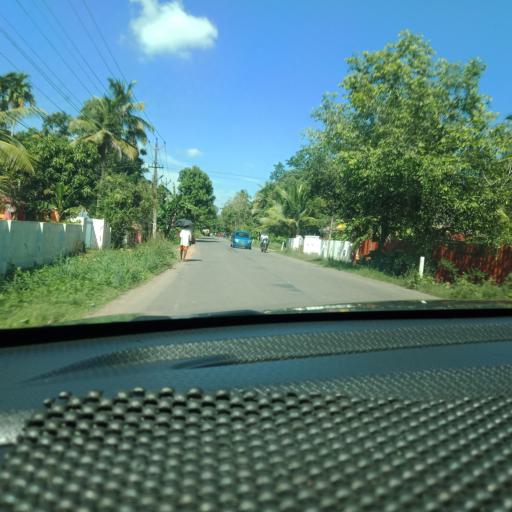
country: IN
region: Kerala
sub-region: Alappuzha
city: Mavelikara
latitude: 9.3031
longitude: 76.4562
